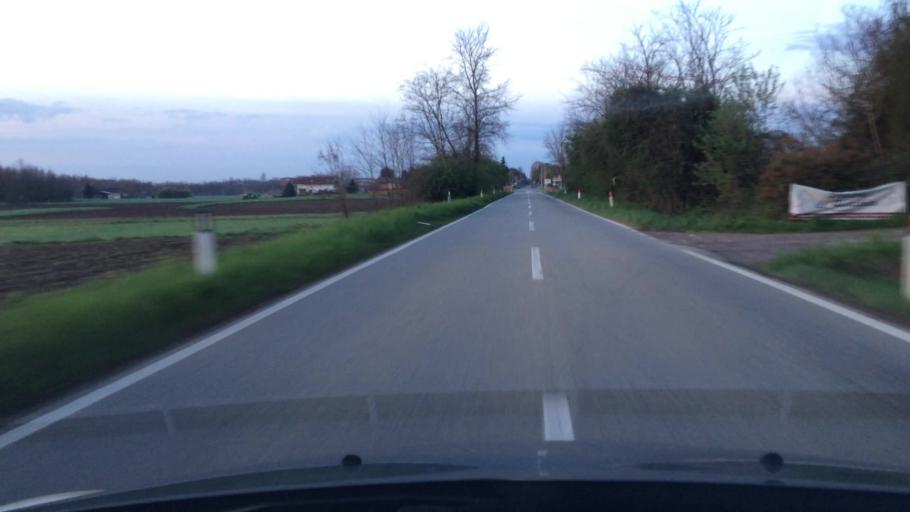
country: IT
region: Lombardy
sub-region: Provincia di Como
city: Puginate
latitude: 45.7107
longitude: 9.0644
